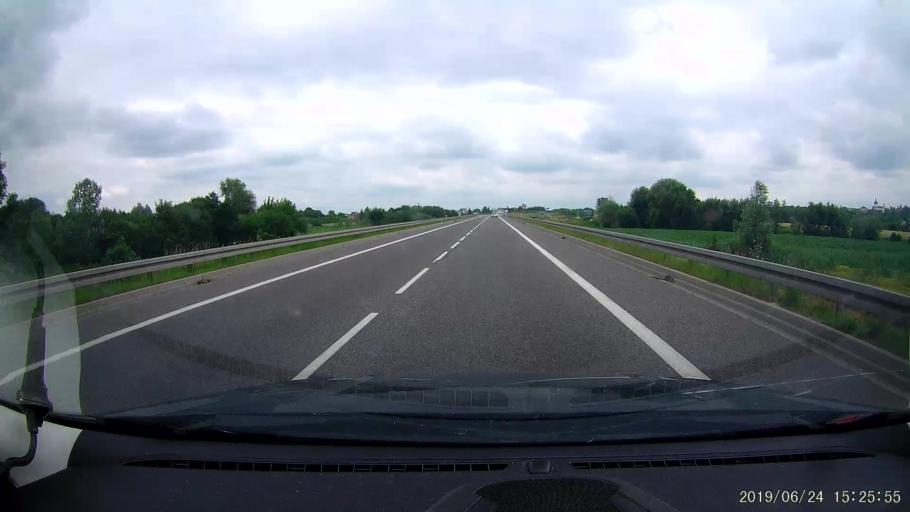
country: PL
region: Subcarpathian Voivodeship
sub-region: Powiat jaroslawski
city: Jaroslaw
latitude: 50.0296
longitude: 22.6870
